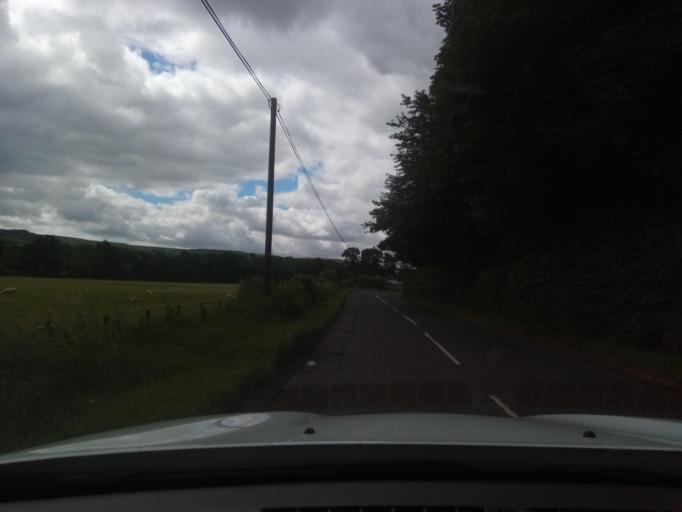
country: GB
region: Scotland
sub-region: The Scottish Borders
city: Selkirk
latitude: 55.5426
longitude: -2.8703
